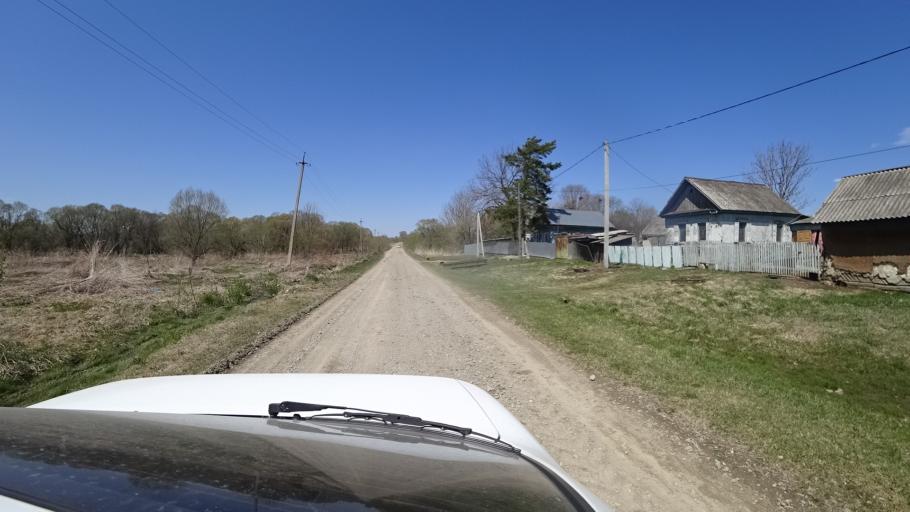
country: RU
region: Primorskiy
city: Lazo
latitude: 45.7938
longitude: 133.7635
